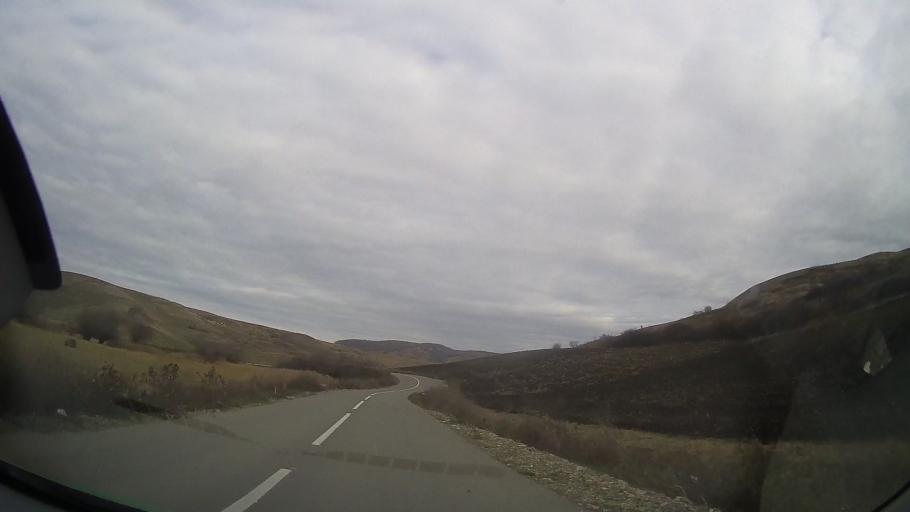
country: RO
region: Bistrita-Nasaud
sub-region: Comuna Silvasu de Campie
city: Silvasu de Campie
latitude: 46.8024
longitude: 24.2991
